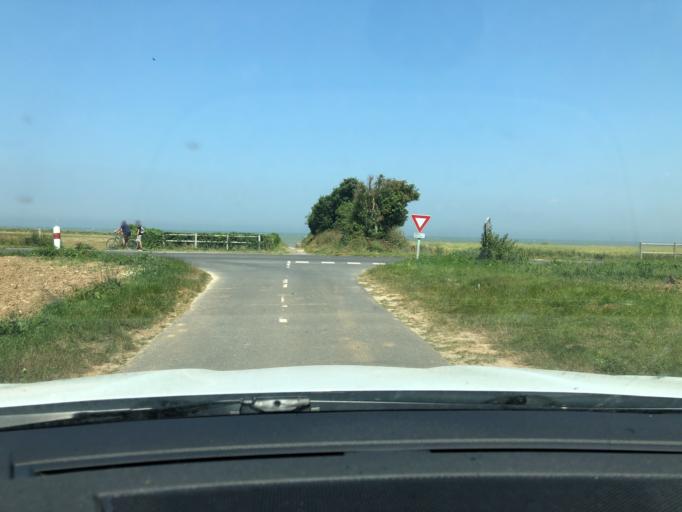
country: FR
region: Lower Normandy
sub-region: Departement du Calvados
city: Lion-sur-Mer
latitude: 49.3073
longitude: -0.3279
